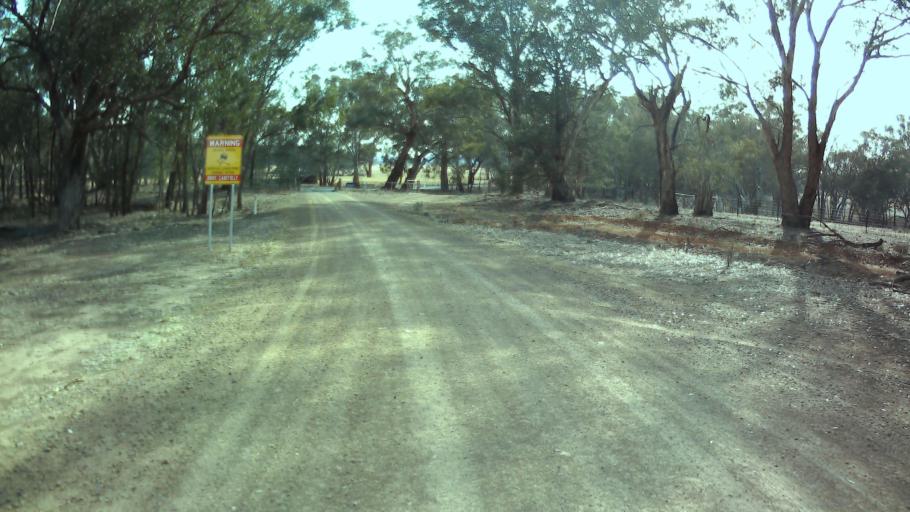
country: AU
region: New South Wales
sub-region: Weddin
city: Grenfell
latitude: -33.7968
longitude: 148.0781
